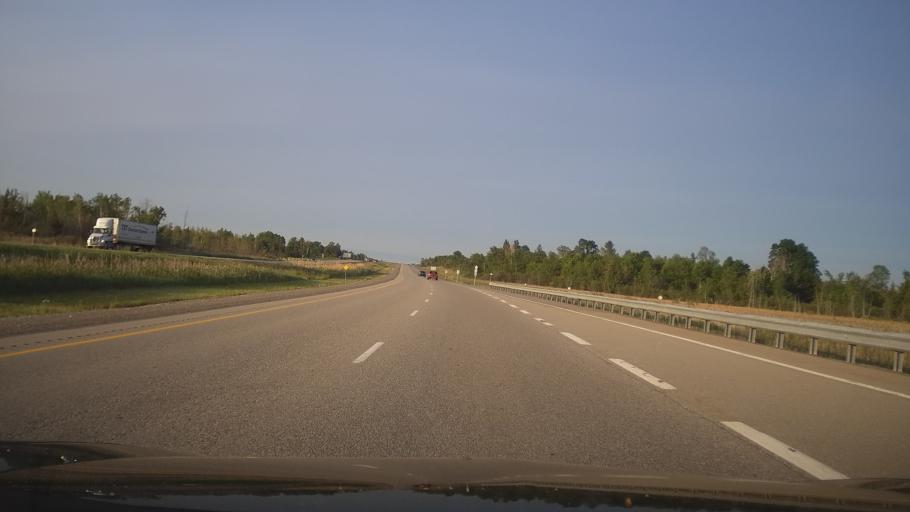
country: CA
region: Ontario
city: Carleton Place
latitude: 45.1962
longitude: -76.0451
